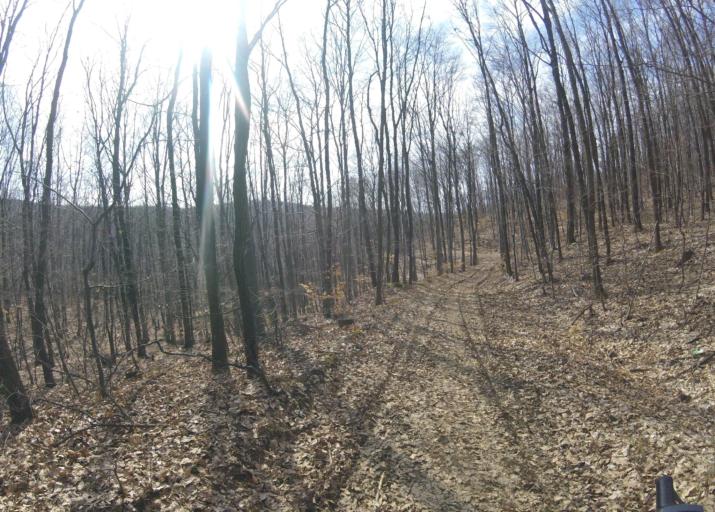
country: HU
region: Heves
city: Belapatfalva
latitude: 48.0251
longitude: 20.3573
